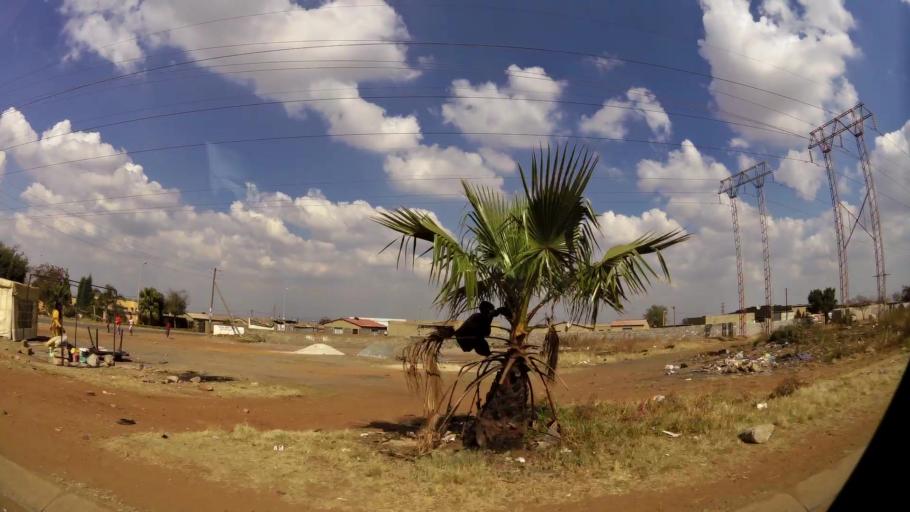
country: ZA
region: Gauteng
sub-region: City of Johannesburg Metropolitan Municipality
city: Roodepoort
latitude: -26.1901
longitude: 27.8607
